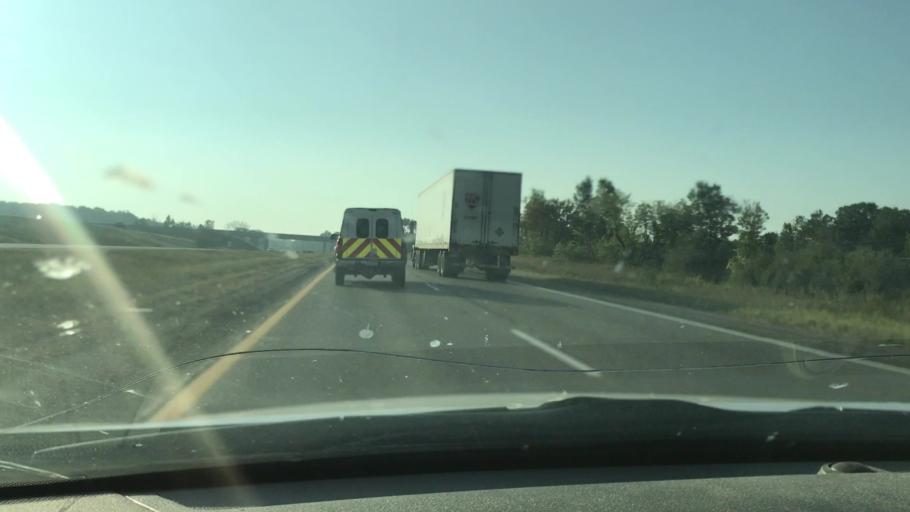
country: US
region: Michigan
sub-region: Livingston County
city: Howell
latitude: 42.6180
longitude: -83.9950
